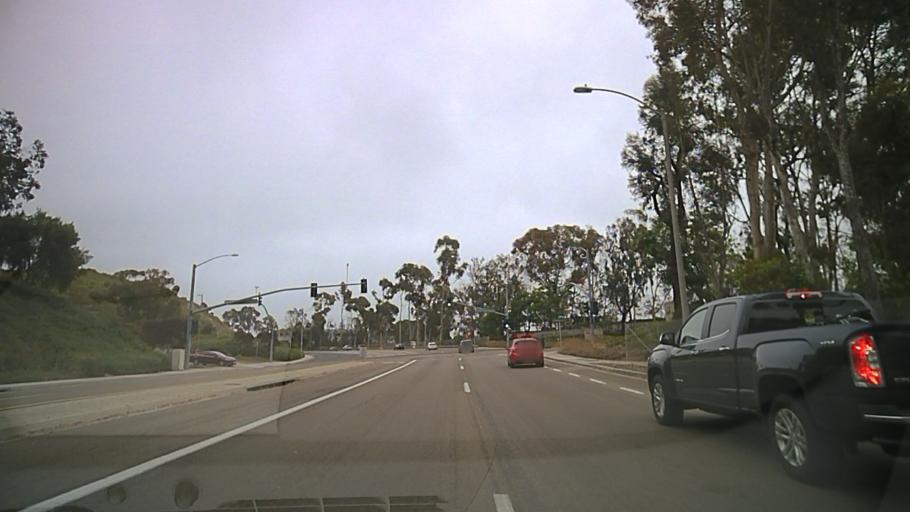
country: US
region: California
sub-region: San Diego County
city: Fairbanks Ranch
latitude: 33.0220
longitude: -117.1052
